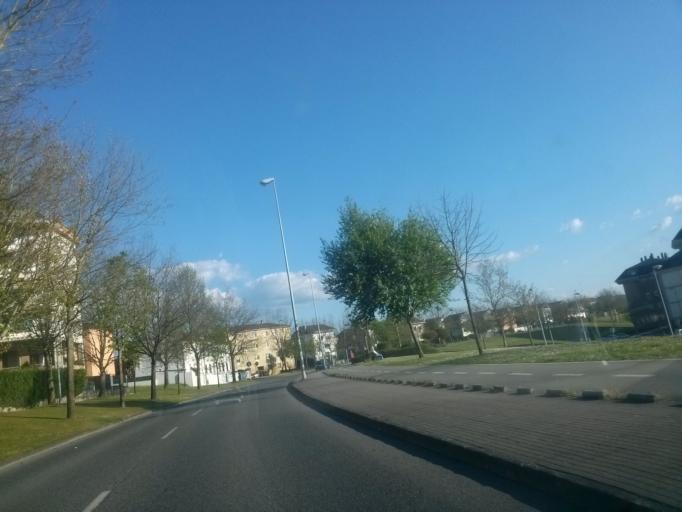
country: ES
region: Galicia
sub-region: Provincia de Lugo
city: Lugo
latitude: 43.0015
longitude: -7.5547
